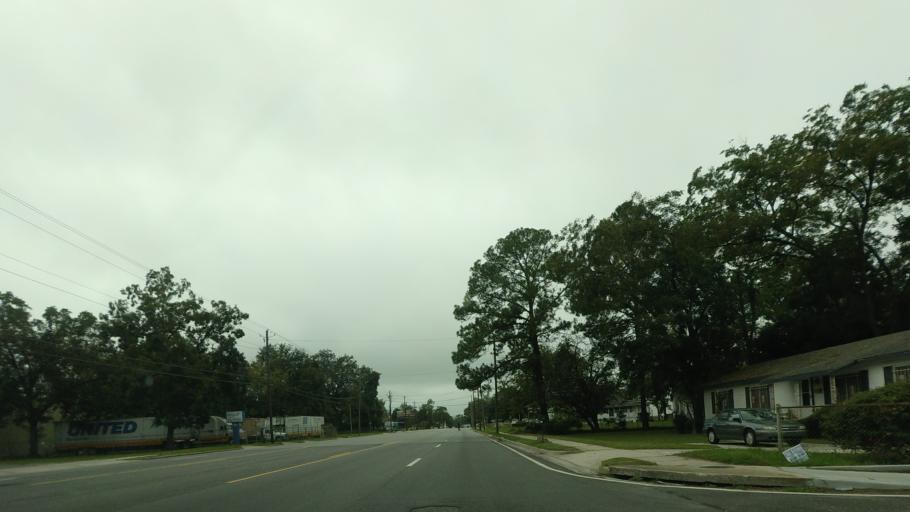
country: US
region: Georgia
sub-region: Lowndes County
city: Valdosta
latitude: 30.8258
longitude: -83.2918
